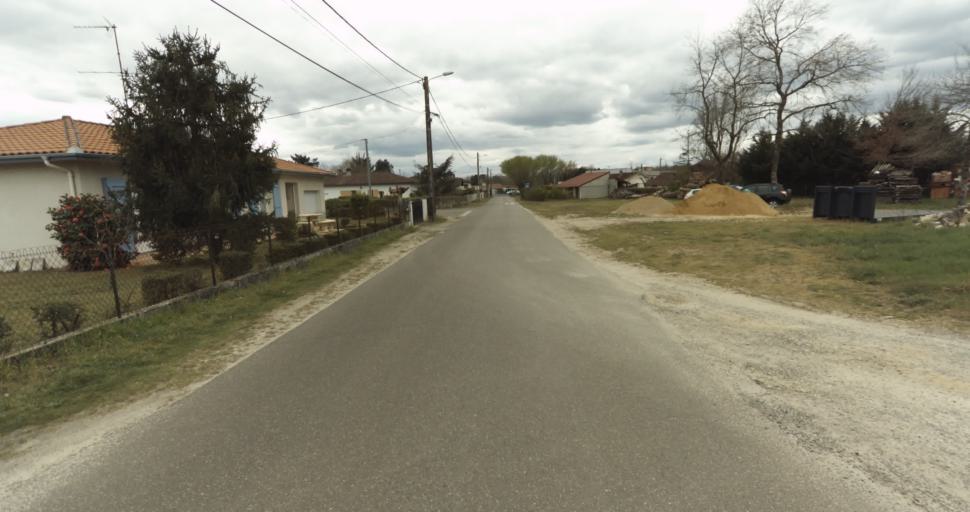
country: FR
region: Aquitaine
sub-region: Departement des Landes
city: Roquefort
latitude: 44.0370
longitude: -0.3125
